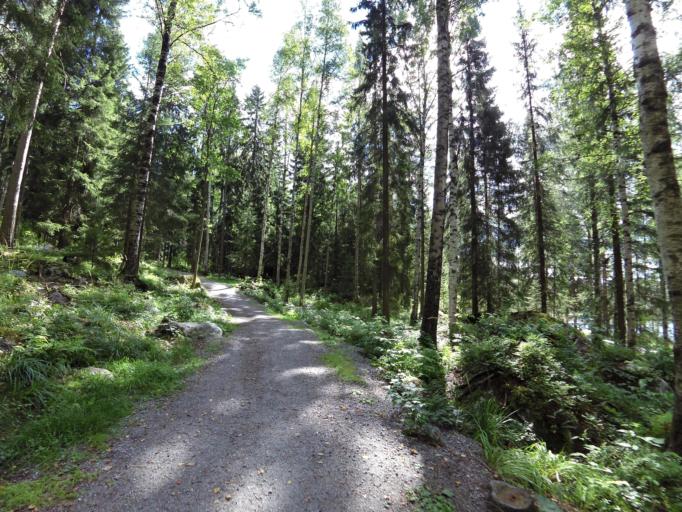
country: FI
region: Pirkanmaa
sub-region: Tampere
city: Pirkkala
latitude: 61.5088
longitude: 23.6166
